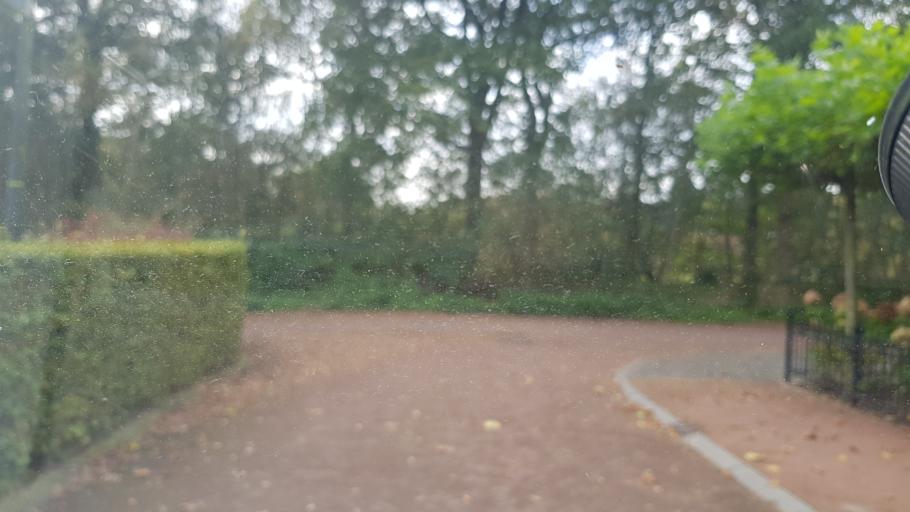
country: NL
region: Gelderland
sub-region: Gemeente Apeldoorn
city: Uddel
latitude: 52.2551
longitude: 5.7820
